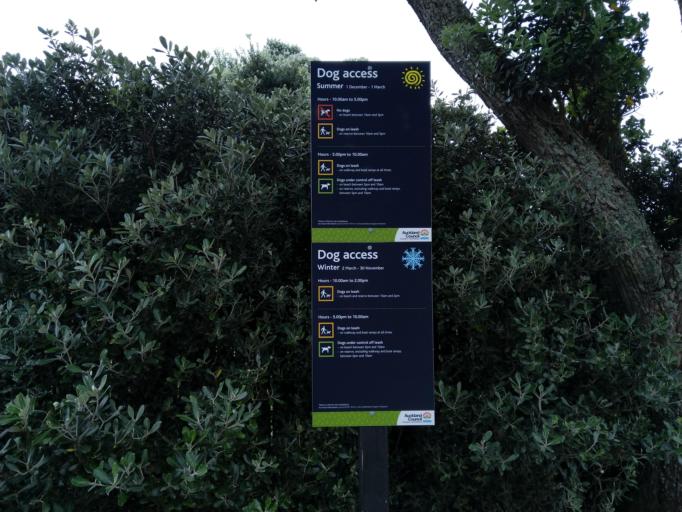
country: NZ
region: Auckland
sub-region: Auckland
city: Auckland
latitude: -36.8232
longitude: 174.8089
